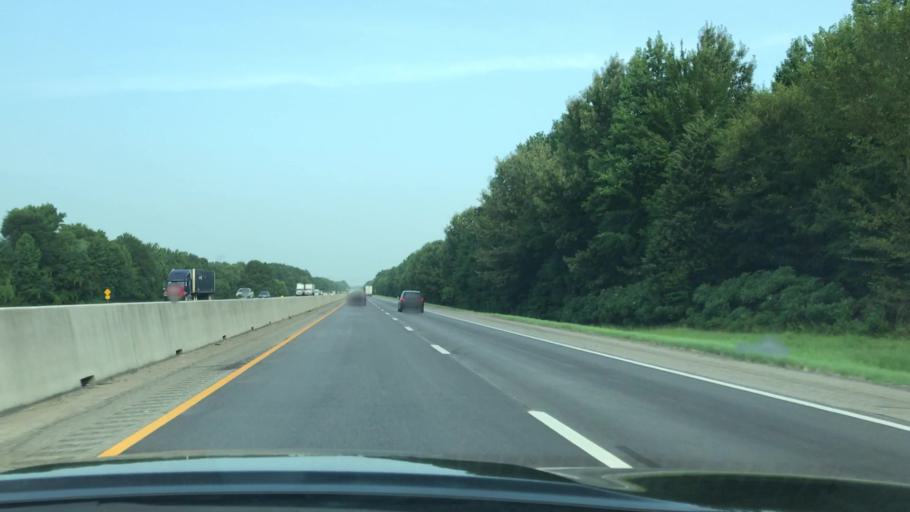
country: US
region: Texas
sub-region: Gregg County
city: Kilgore
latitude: 32.4326
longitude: -94.8767
